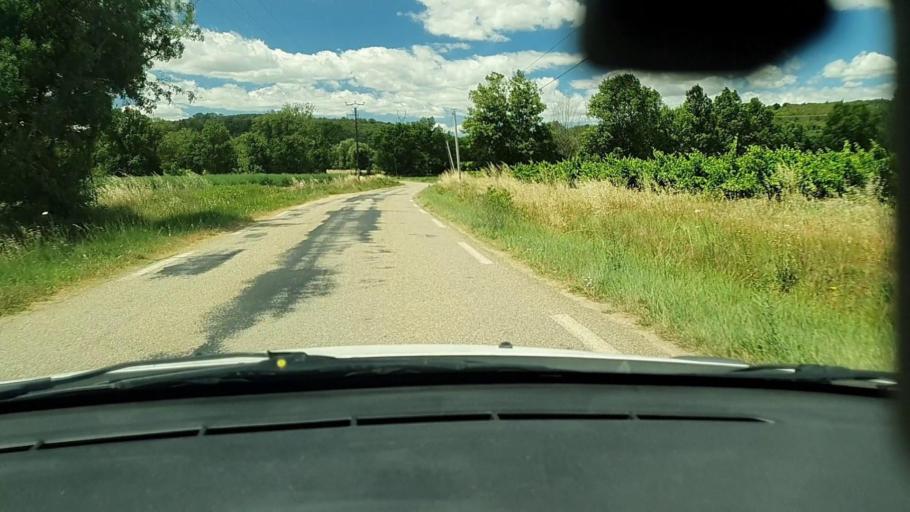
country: FR
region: Languedoc-Roussillon
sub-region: Departement du Gard
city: Blauzac
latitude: 43.9496
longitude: 4.3864
